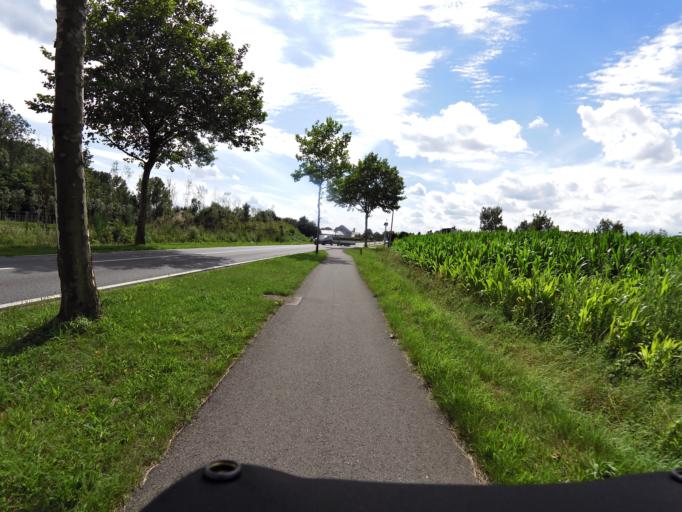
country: BE
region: Flanders
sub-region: Provincie Antwerpen
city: Hoogstraten
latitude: 51.4299
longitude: 4.7648
